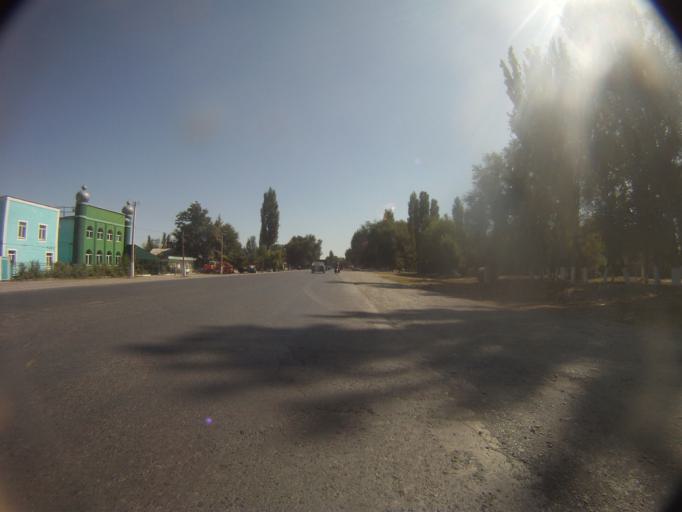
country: KG
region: Chuy
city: Kara-Balta
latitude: 42.8343
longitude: 73.9077
